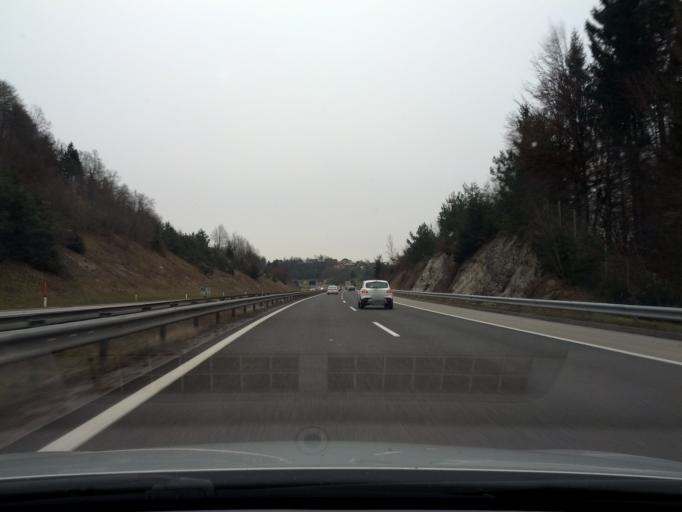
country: SI
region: Skofljica
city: Skofljica
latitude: 45.9938
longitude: 14.5911
